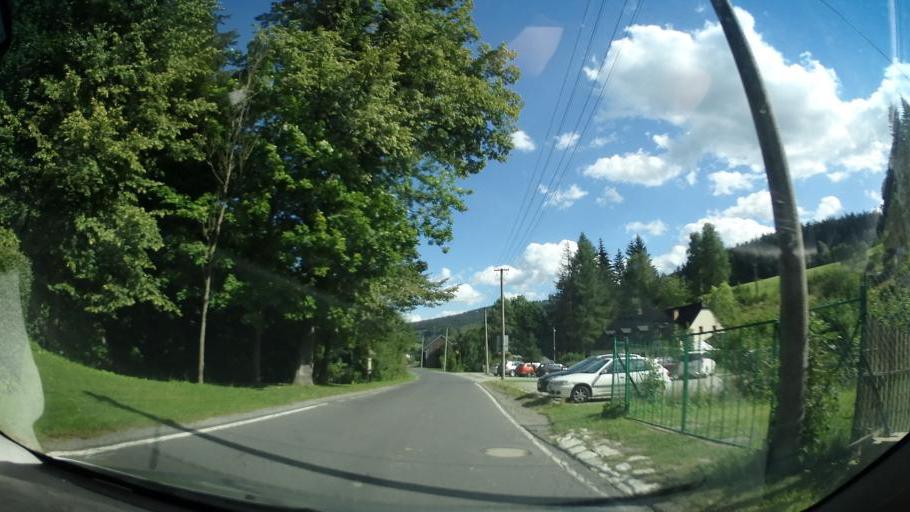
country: CZ
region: Olomoucky
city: Vapenna
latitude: 50.2246
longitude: 17.0928
